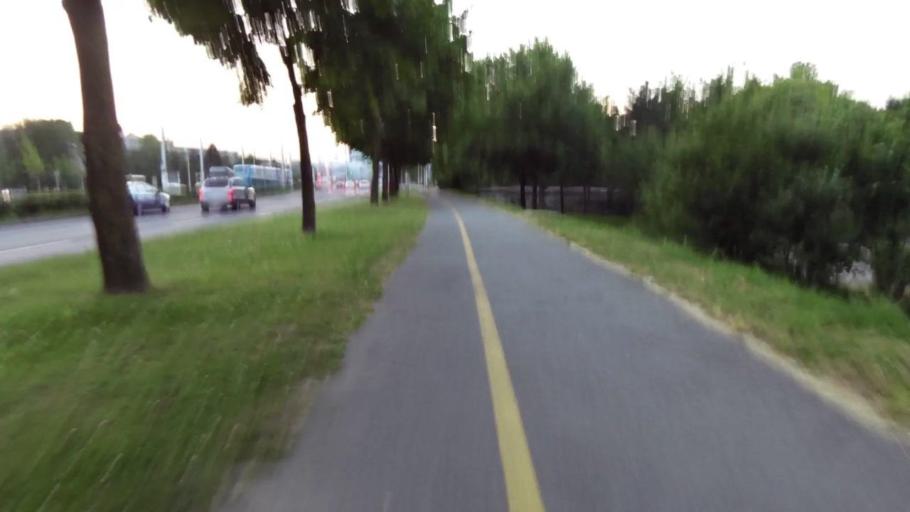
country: HR
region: Grad Zagreb
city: Novi Zagreb
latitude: 45.7903
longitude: 16.0040
